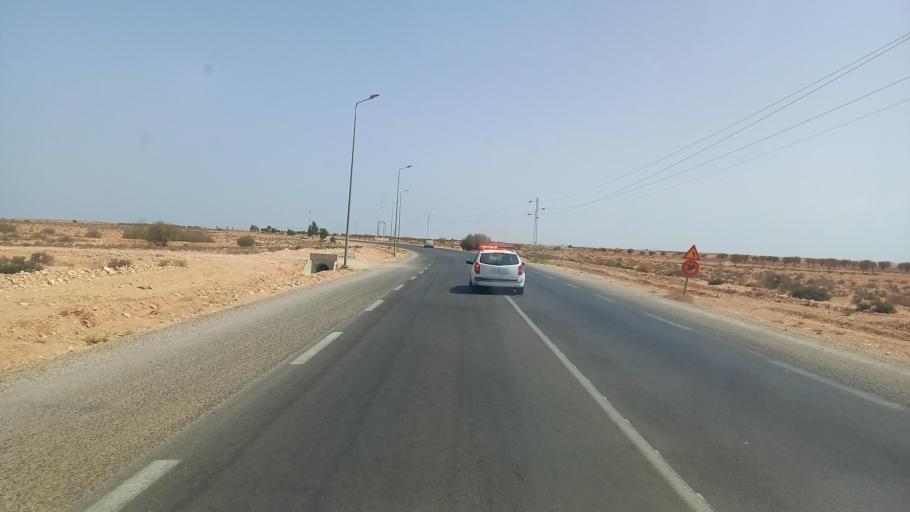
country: TN
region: Madanin
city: Medenine
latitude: 33.3760
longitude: 10.6957
